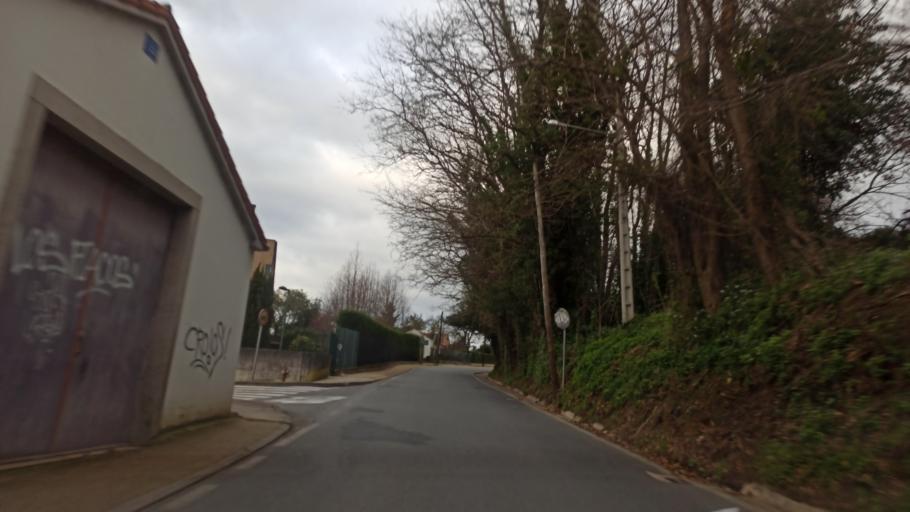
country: ES
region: Galicia
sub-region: Provincia da Coruna
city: Oleiros
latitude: 43.3365
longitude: -8.3516
